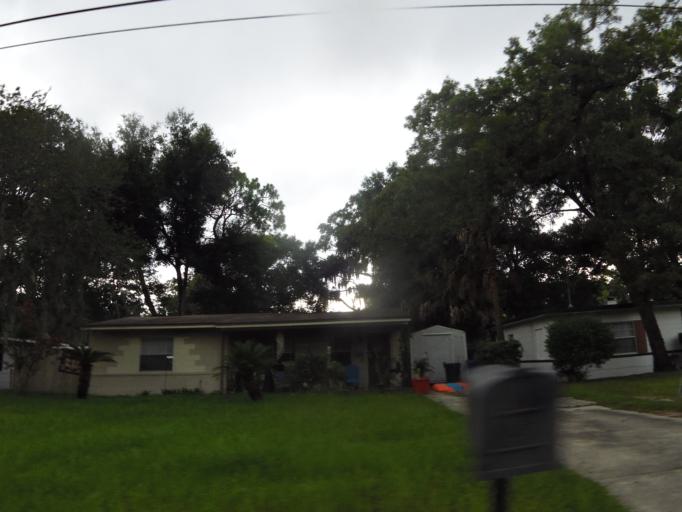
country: US
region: Florida
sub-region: Duval County
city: Jacksonville
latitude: 30.3422
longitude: -81.6039
